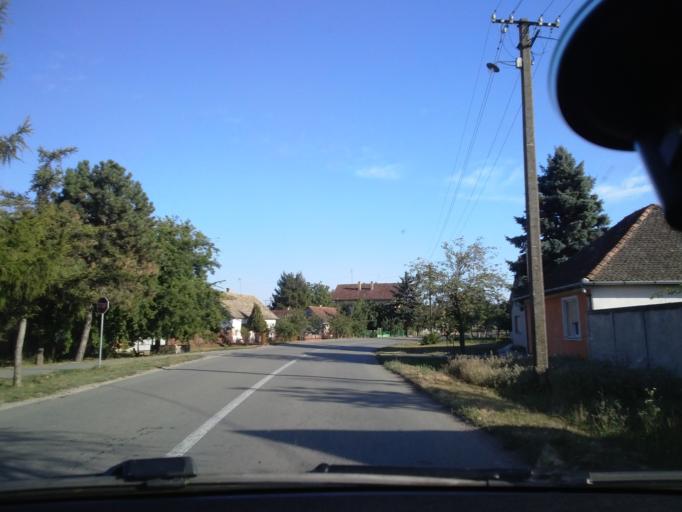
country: RS
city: Doroslovo
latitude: 45.5953
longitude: 19.1919
